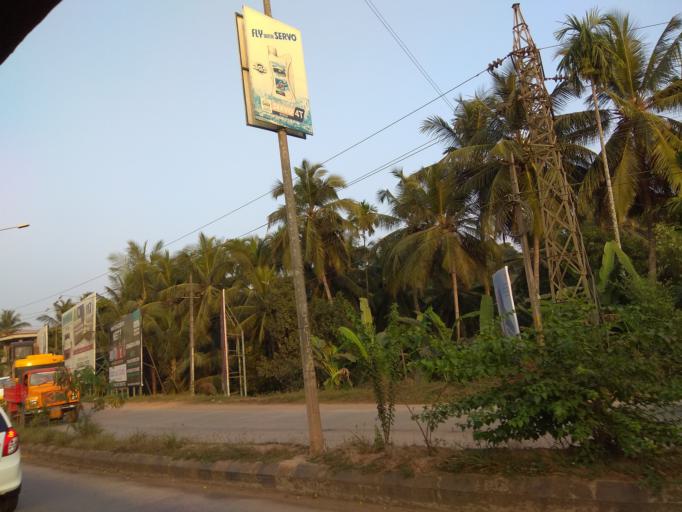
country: IN
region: Karnataka
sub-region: Dakshina Kannada
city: Mangalore
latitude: 12.9314
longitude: 74.8586
